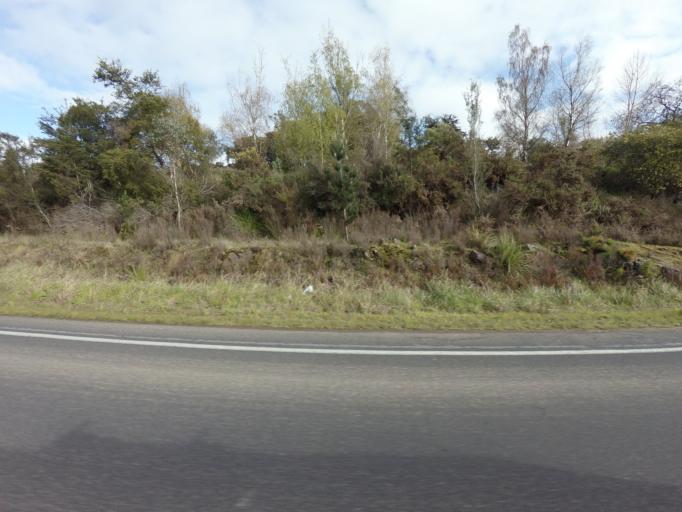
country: AU
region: Tasmania
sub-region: Huon Valley
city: Franklin
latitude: -43.0695
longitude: 147.0236
